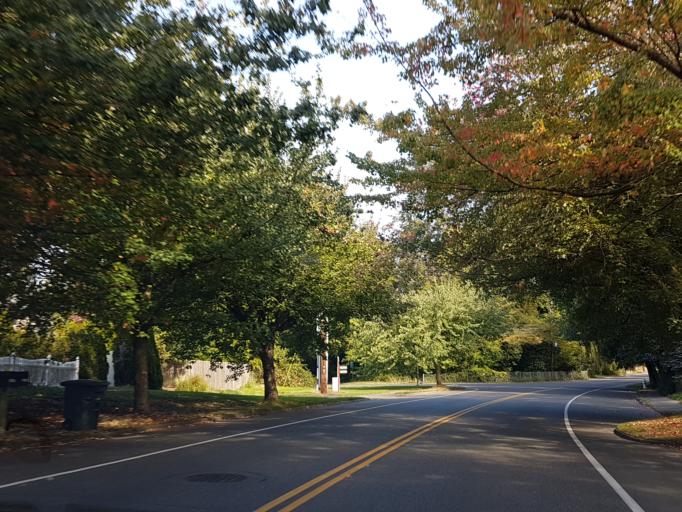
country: US
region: Washington
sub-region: Snohomish County
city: Brier
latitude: 47.7706
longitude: -122.2639
